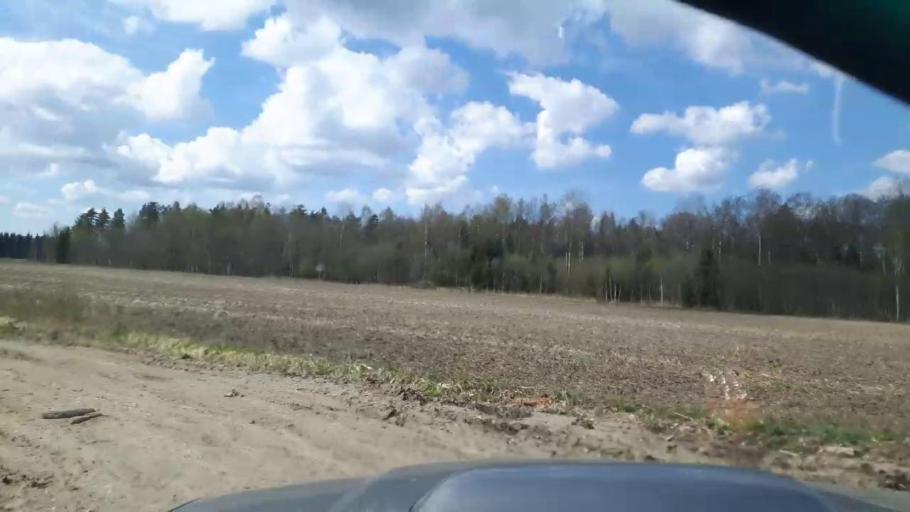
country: EE
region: Paernumaa
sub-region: Vaendra vald (alev)
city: Vandra
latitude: 58.5445
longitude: 25.0707
